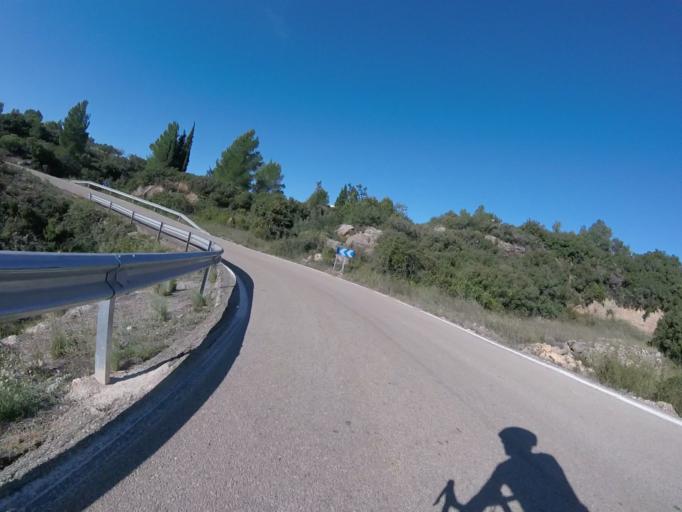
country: ES
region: Valencia
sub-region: Provincia de Castello
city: Chert/Xert
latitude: 40.4500
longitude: 0.1123
